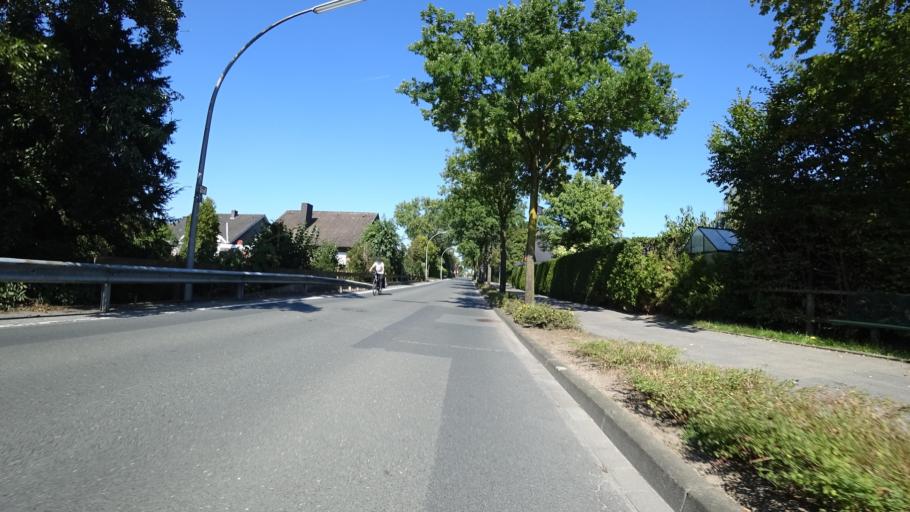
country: DE
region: North Rhine-Westphalia
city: Oelde
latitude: 51.8220
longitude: 8.1316
